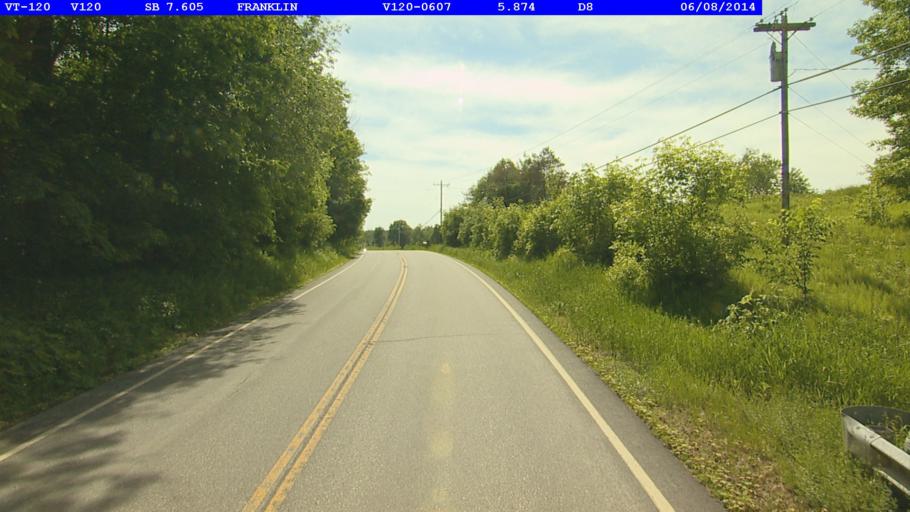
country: US
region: Vermont
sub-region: Franklin County
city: Enosburg Falls
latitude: 44.9892
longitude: -72.8769
